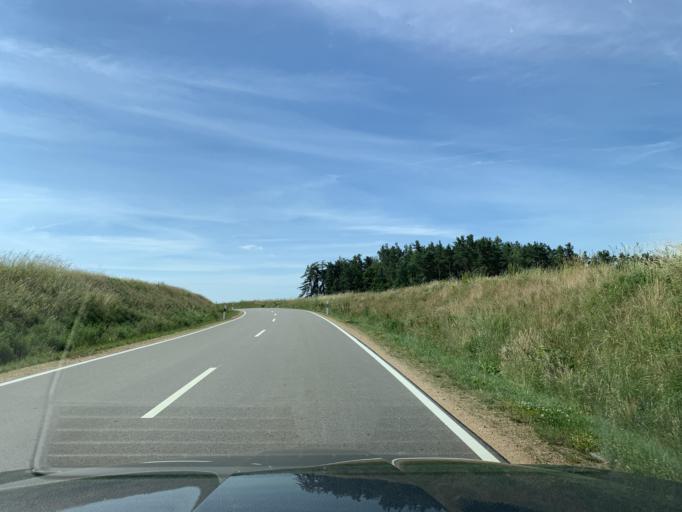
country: DE
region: Bavaria
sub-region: Upper Palatinate
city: Pettendorf
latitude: 49.3448
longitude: 12.3299
